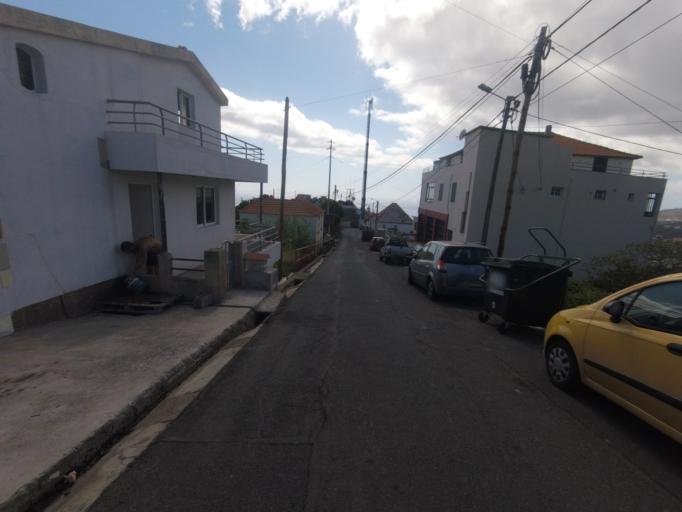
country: PT
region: Madeira
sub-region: Ribeira Brava
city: Campanario
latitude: 32.6745
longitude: -17.0507
